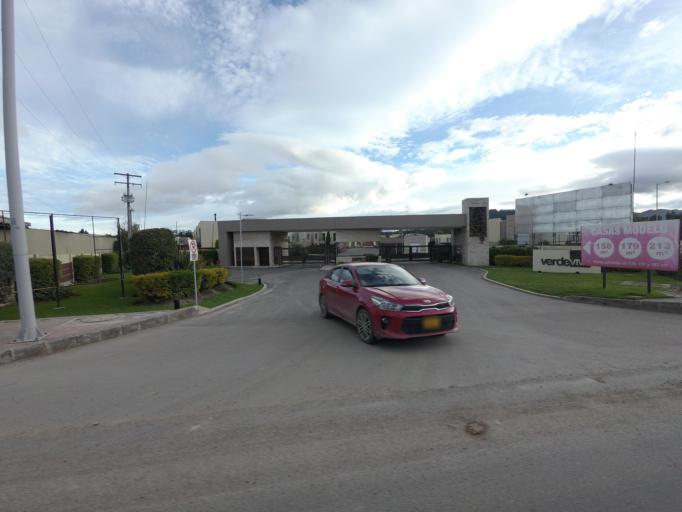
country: CO
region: Cundinamarca
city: Cajica
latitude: 4.9247
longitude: -74.0470
